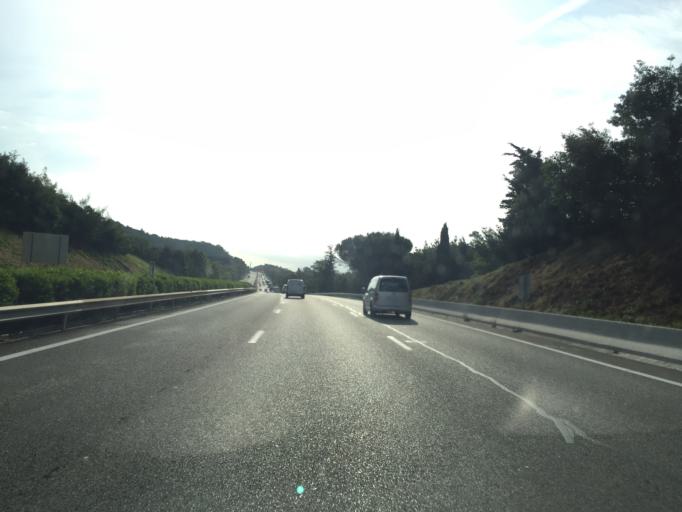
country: FR
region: Provence-Alpes-Cote d'Azur
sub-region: Departement des Alpes-Maritimes
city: Mandelieu-la-Napoule
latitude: 43.5357
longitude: 6.8882
